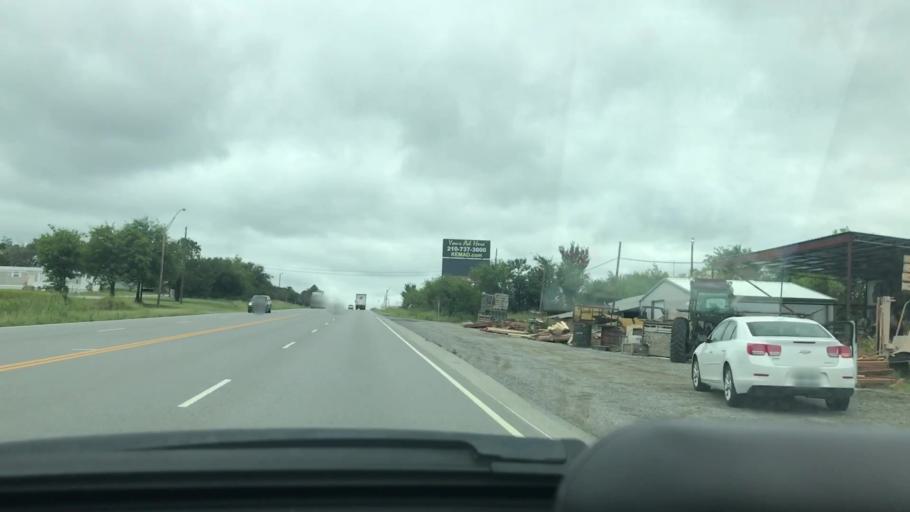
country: US
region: Oklahoma
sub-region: Pittsburg County
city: McAlester
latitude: 34.8395
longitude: -95.8340
